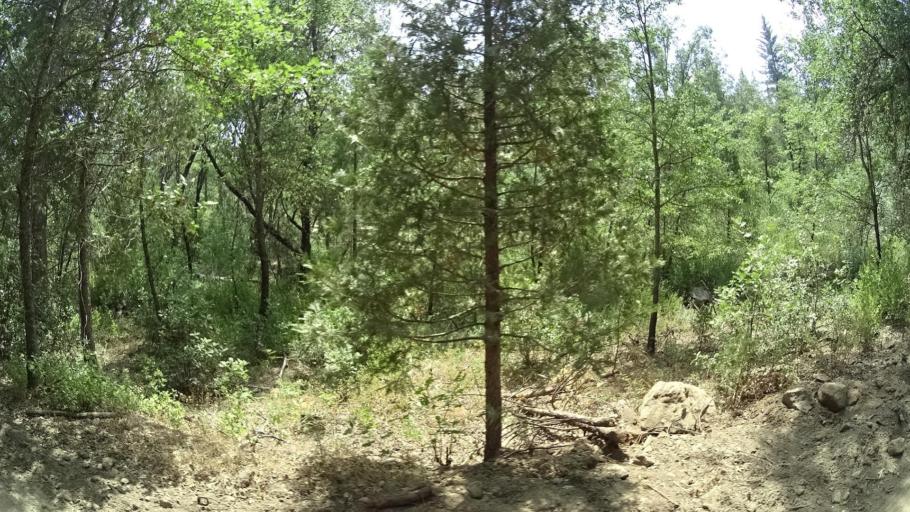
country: US
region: California
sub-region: Mariposa County
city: Midpines
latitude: 37.7401
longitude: -120.0787
